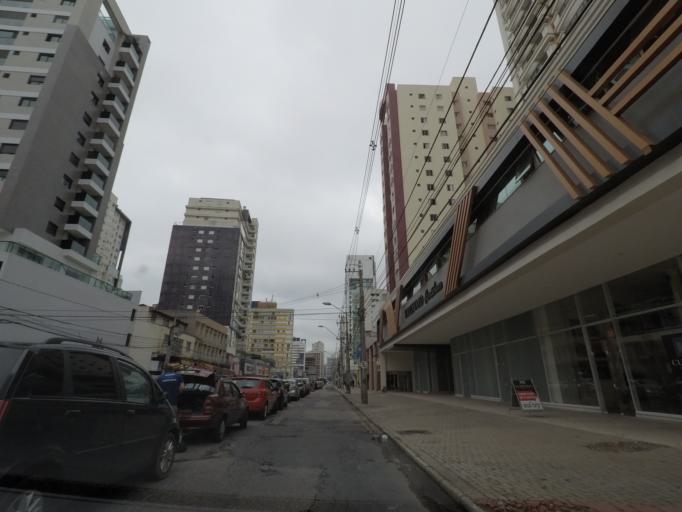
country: BR
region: Parana
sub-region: Curitiba
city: Curitiba
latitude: -25.4553
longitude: -49.2883
